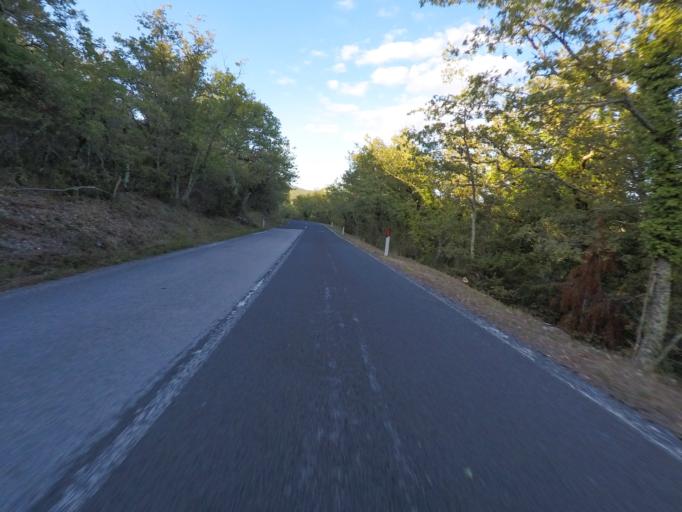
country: IT
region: Tuscany
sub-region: Provincia di Siena
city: Radda in Chianti
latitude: 43.4586
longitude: 11.3869
